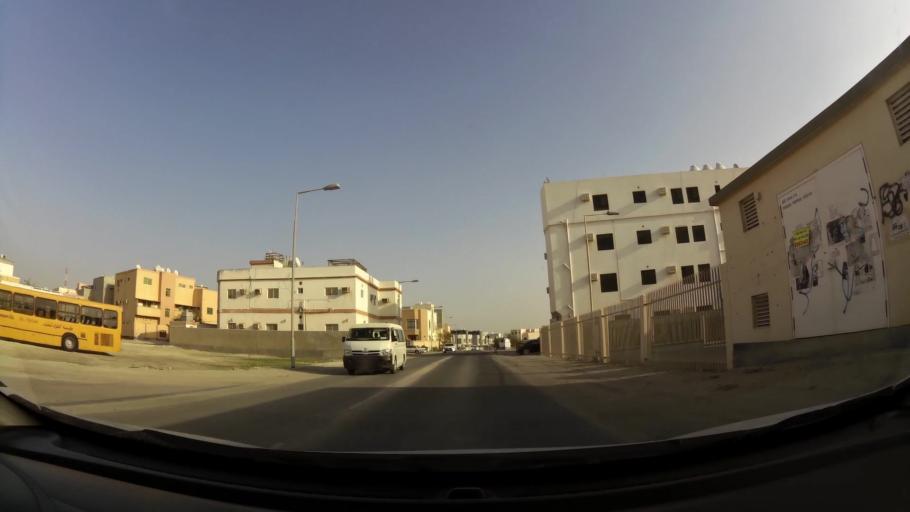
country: BH
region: Manama
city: Jidd Hafs
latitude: 26.2116
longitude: 50.5014
